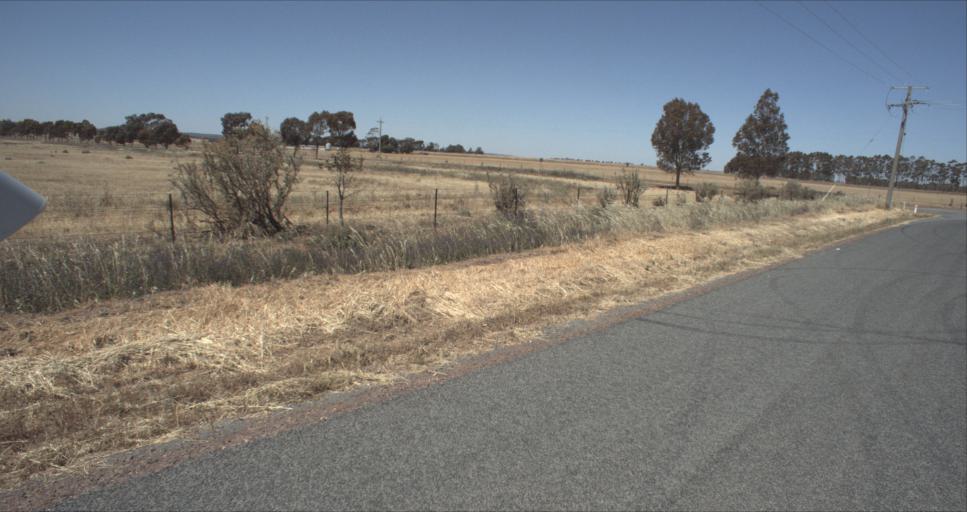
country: AU
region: New South Wales
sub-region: Leeton
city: Leeton
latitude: -34.5331
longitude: 146.4466
